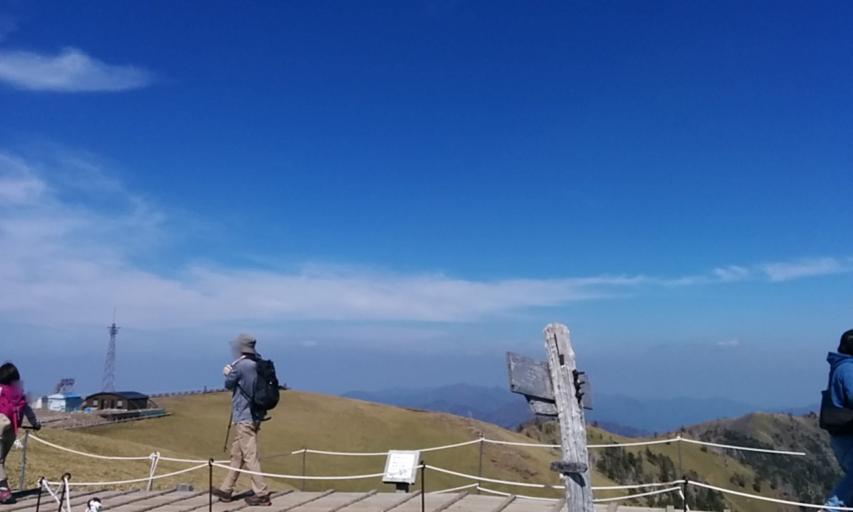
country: JP
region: Tokushima
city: Wakimachi
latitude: 33.8536
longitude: 134.0943
